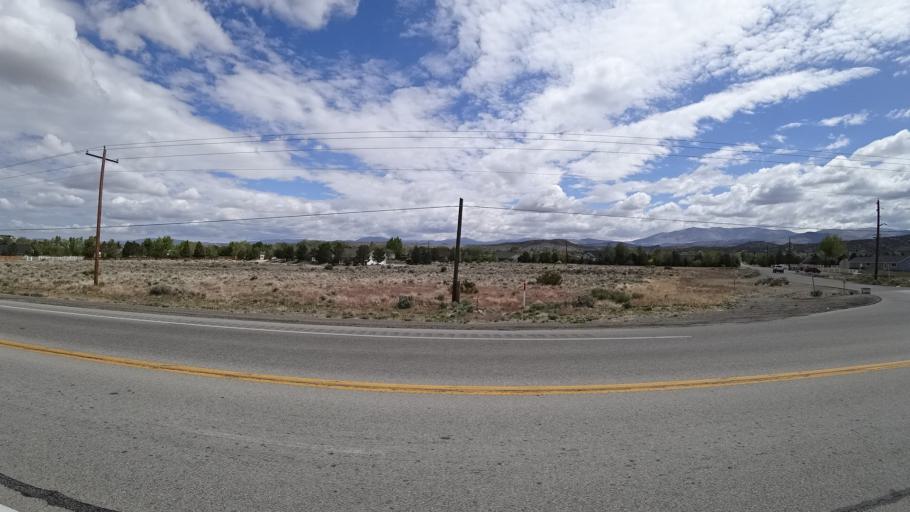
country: US
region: Nevada
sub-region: Douglas County
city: Gardnerville Ranchos
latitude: 38.8853
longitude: -119.6932
